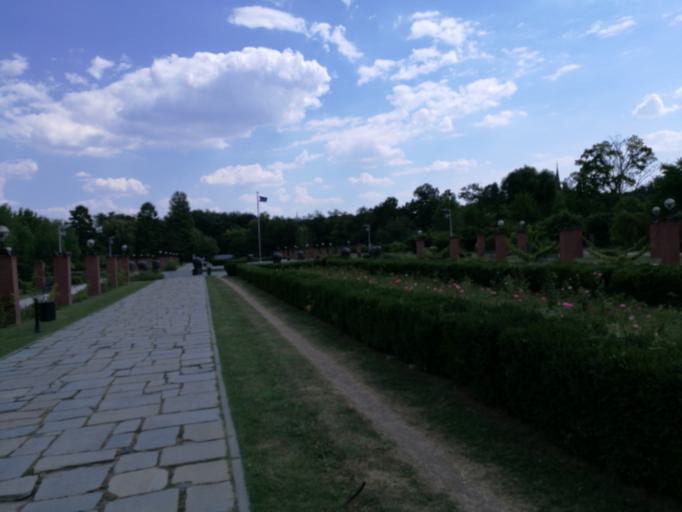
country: RO
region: Bucuresti
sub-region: Municipiul Bucuresti
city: Bucuresti
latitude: 44.4735
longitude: 26.0785
